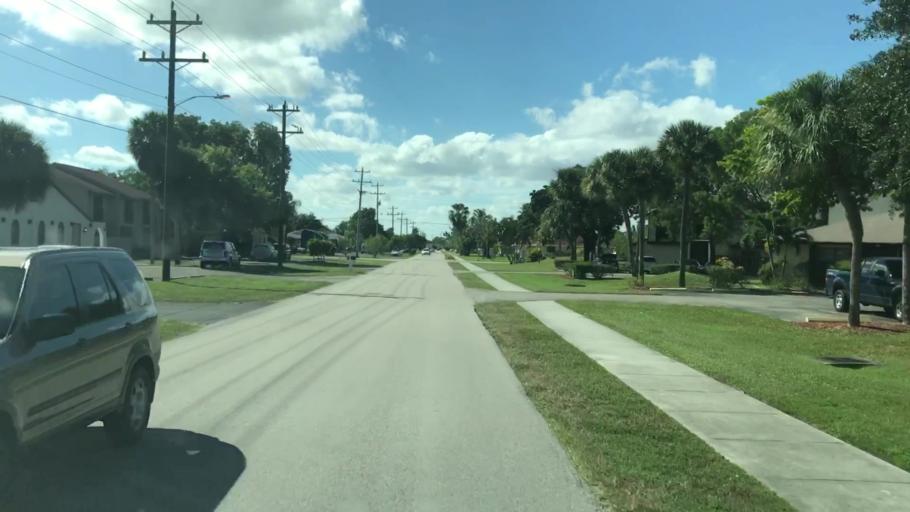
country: US
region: Florida
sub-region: Lee County
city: Lochmoor Waterway Estates
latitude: 26.6379
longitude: -81.9498
